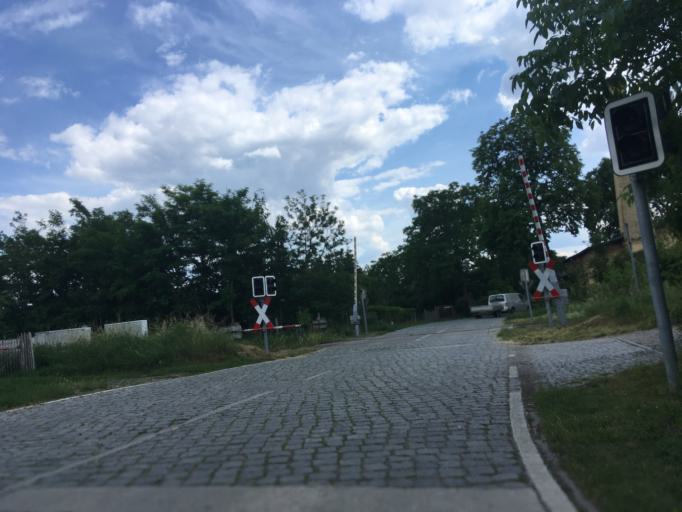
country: DE
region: Brandenburg
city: Muncheberg
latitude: 52.5261
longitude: 14.1046
